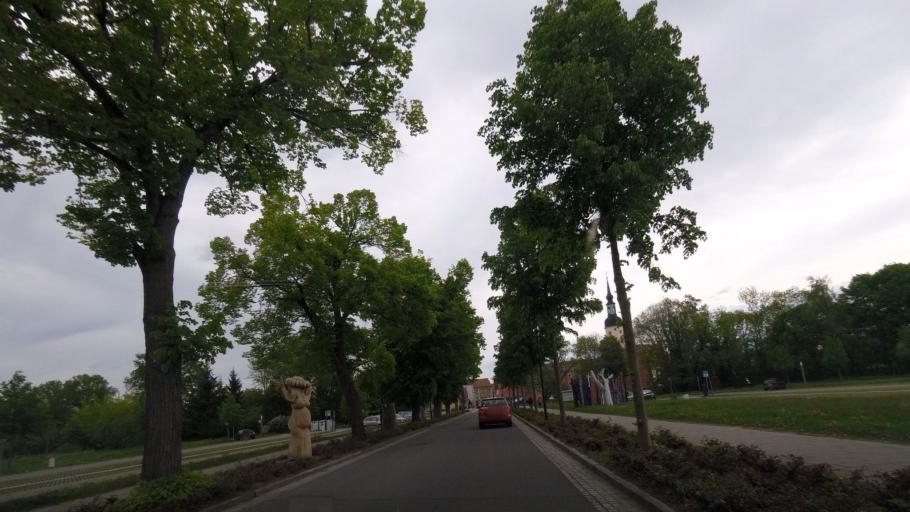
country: DE
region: Brandenburg
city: Lubbenau
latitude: 51.8666
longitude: 13.9665
